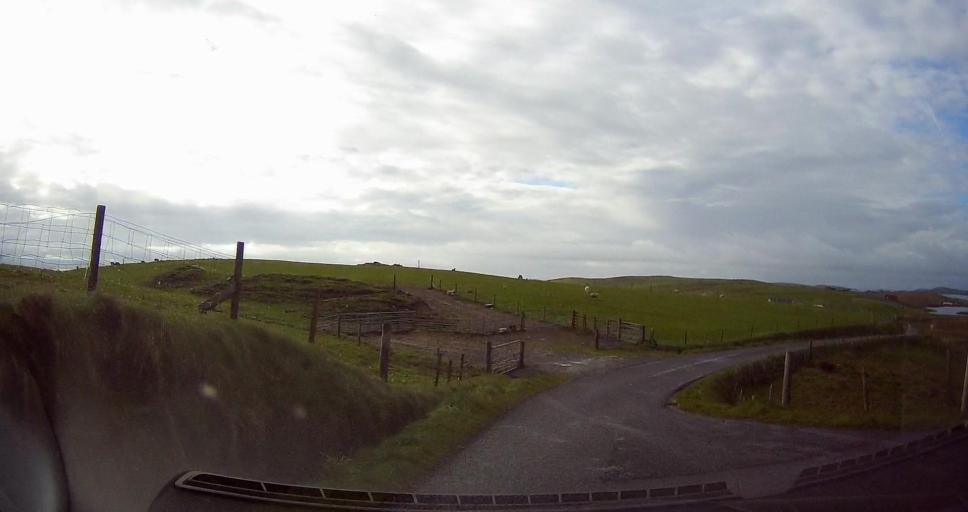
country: GB
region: Scotland
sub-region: Shetland Islands
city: Sandwick
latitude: 60.0537
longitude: -1.2078
